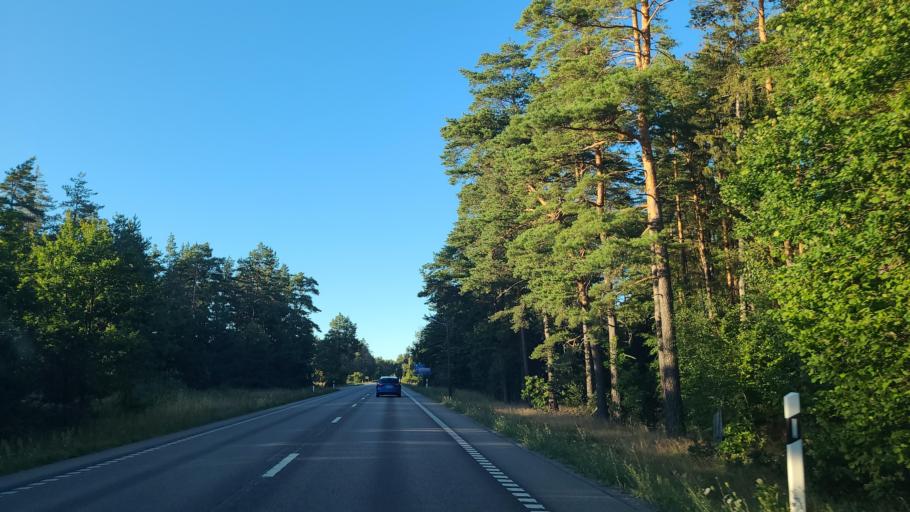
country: SE
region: Kalmar
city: Faerjestaden
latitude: 56.7587
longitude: 16.5577
